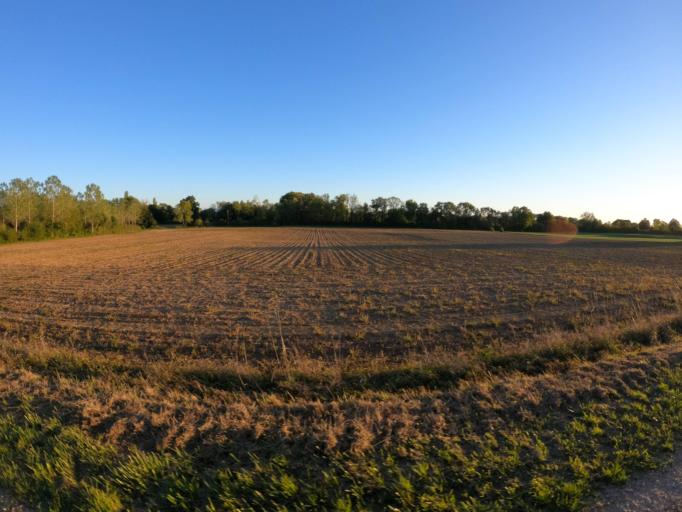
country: FR
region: Franche-Comte
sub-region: Departement du Jura
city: Bletterans
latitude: 46.7442
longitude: 5.4158
